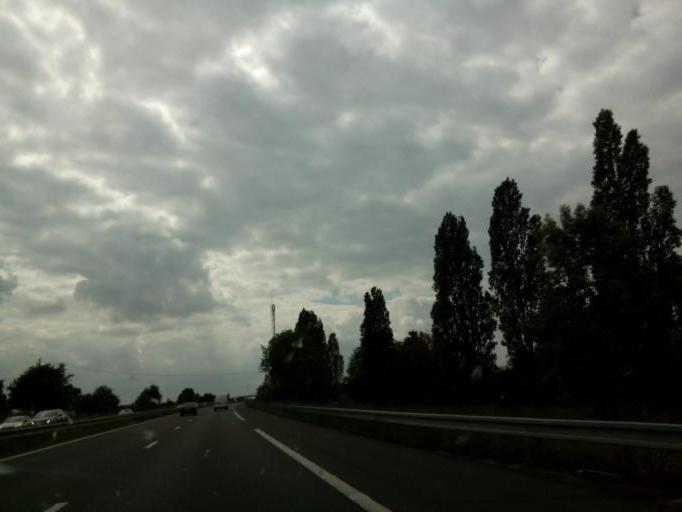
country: FR
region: Pays de la Loire
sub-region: Departement de Maine-et-Loire
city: Champtoce-sur-Loire
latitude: 47.4315
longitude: -0.8811
